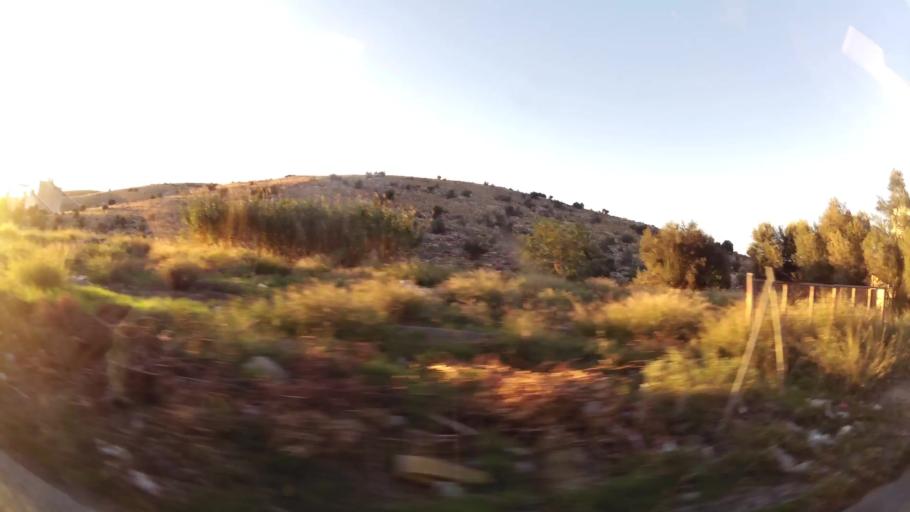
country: GR
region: Attica
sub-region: Nomarchia Athinas
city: Petroupolis
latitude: 38.0489
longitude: 23.6402
